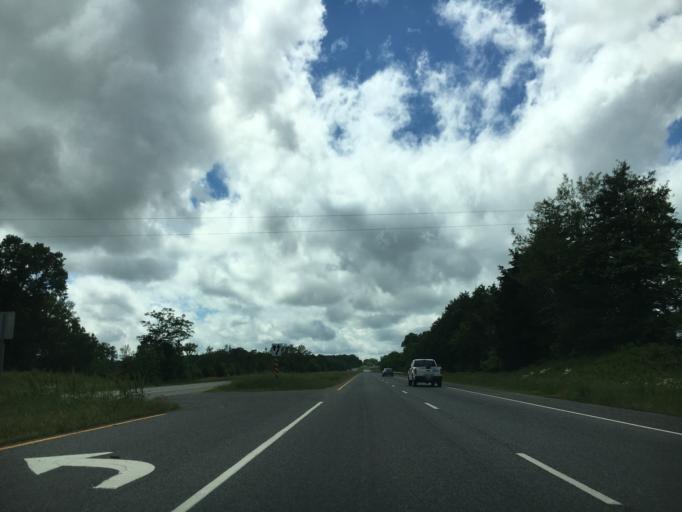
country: US
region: Virginia
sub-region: Mecklenburg County
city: Boydton
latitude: 36.6525
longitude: -78.4697
